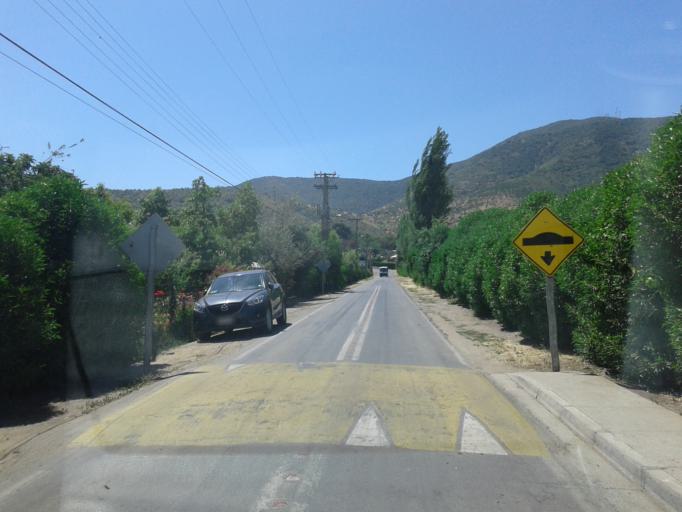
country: CL
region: Valparaiso
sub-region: Provincia de Quillota
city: Hacienda La Calera
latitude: -32.8371
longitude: -71.1942
